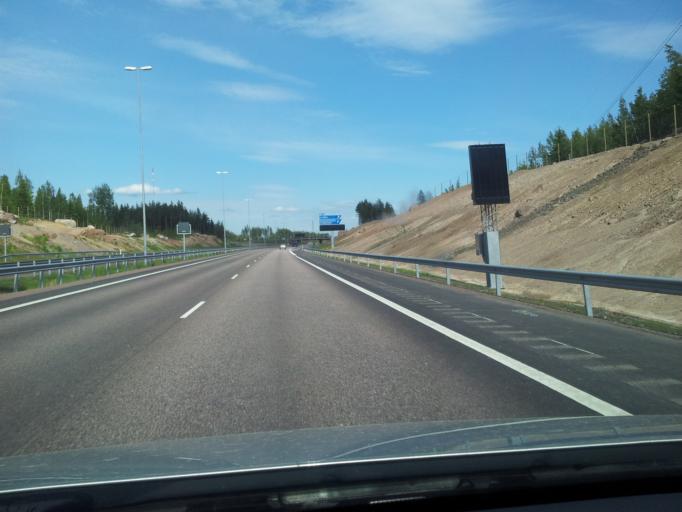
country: FI
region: Uusimaa
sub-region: Loviisa
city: Ruotsinpyhtaeae
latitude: 60.4898
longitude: 26.4071
